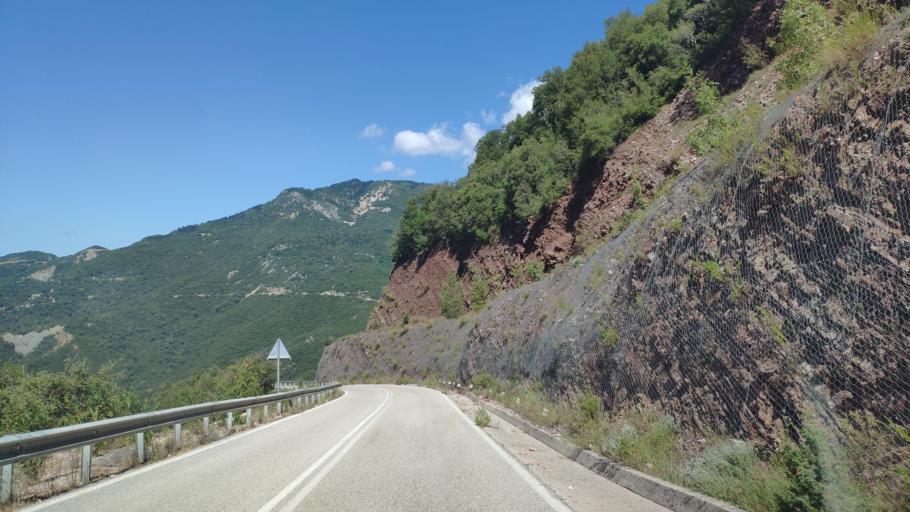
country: GR
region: Central Greece
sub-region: Nomos Evrytanias
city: Kerasochori
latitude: 39.0132
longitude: 21.5981
